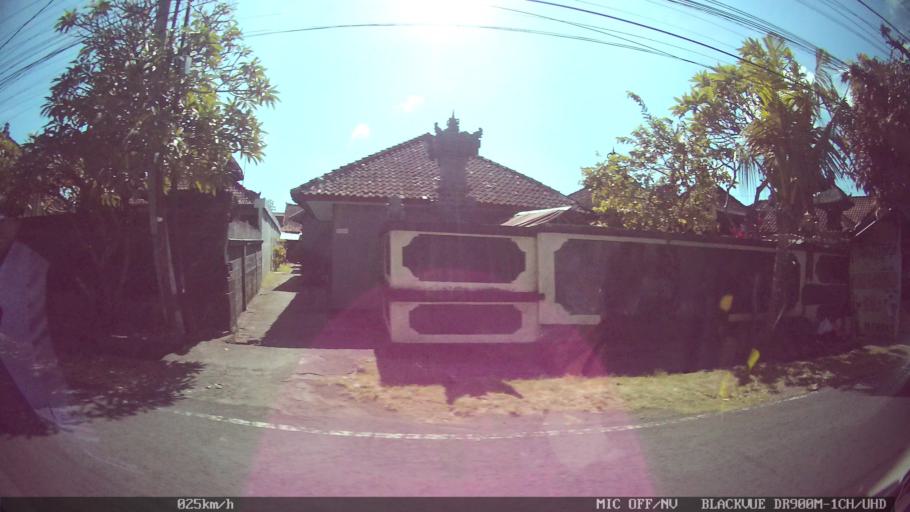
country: ID
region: Bali
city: Denpasar
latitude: -8.6534
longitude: 115.1774
